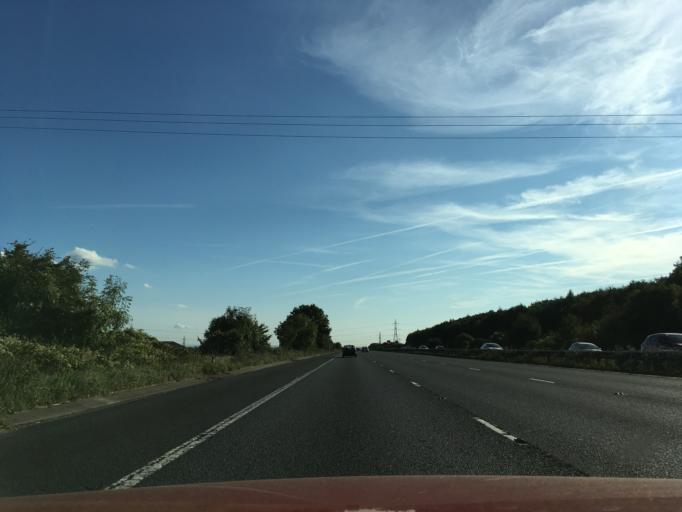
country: GB
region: England
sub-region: South Gloucestershire
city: Tytherington
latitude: 51.5945
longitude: -2.4882
